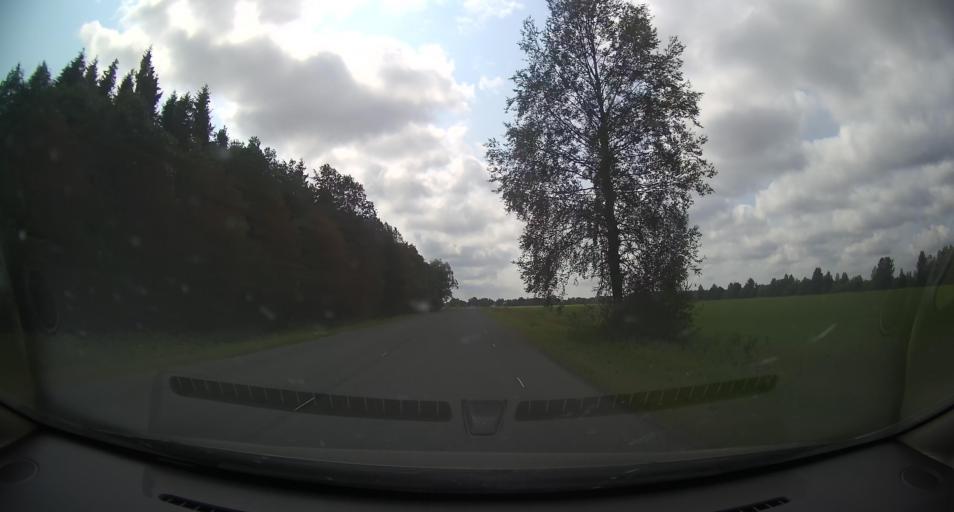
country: EE
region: Paernumaa
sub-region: Audru vald
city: Audru
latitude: 58.4847
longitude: 24.3348
